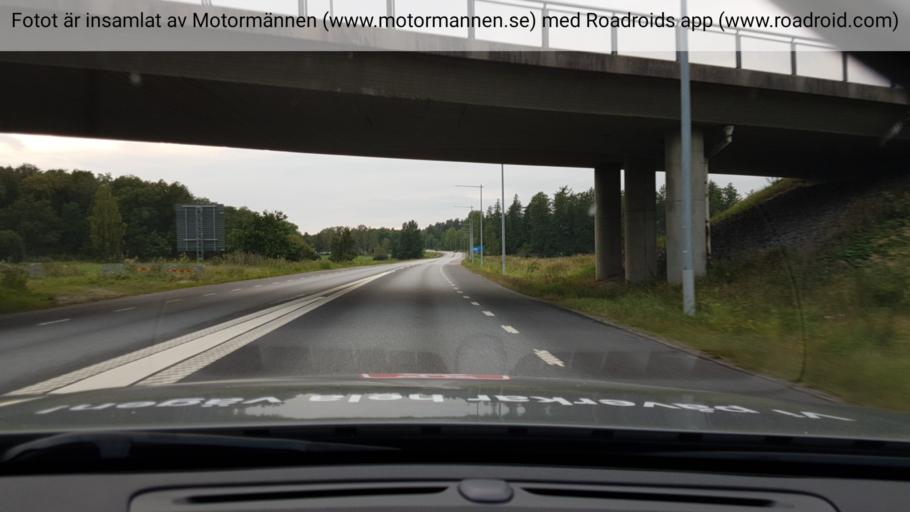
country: SE
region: Vaestmanland
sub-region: Arboga Kommun
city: Arboga
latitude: 59.3886
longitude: 15.8367
